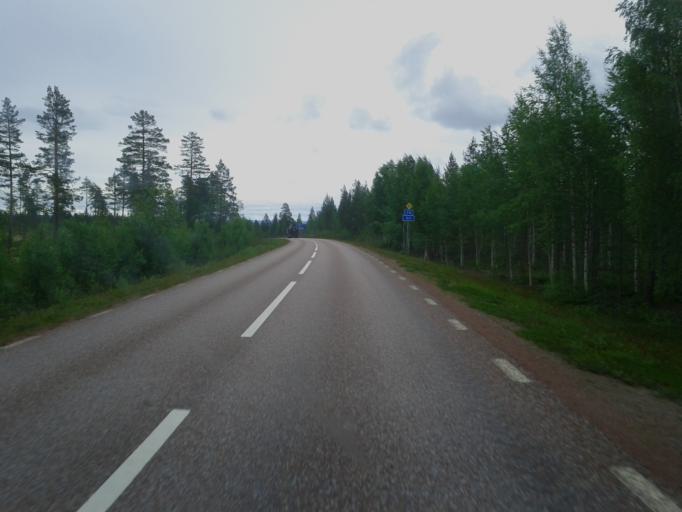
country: NO
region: Hedmark
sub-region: Trysil
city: Innbygda
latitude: 61.6925
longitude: 13.0624
